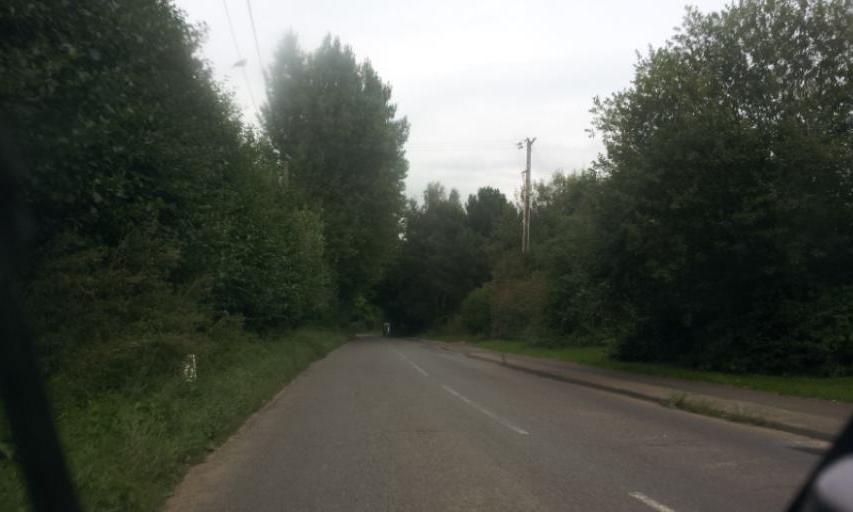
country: GB
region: England
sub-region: Kent
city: East Peckham
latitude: 51.2124
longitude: 0.3762
